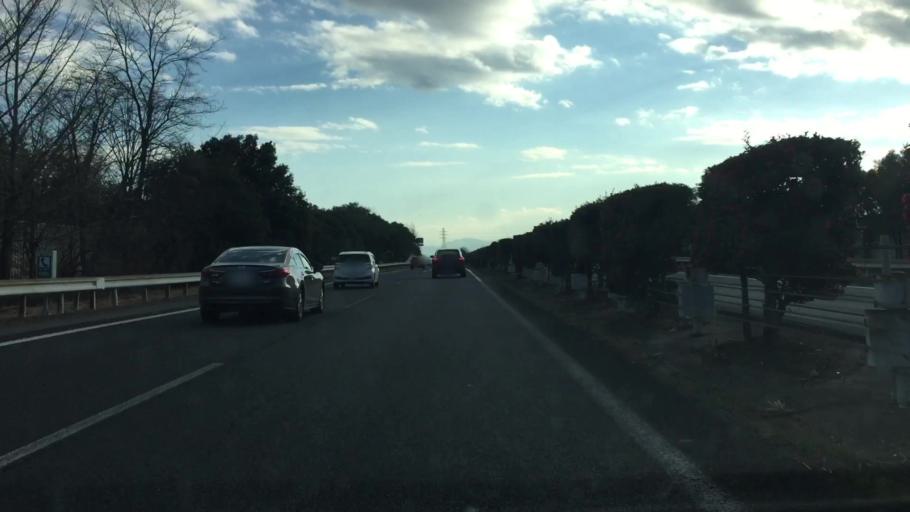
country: JP
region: Gunma
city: Kanekomachi
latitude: 36.4428
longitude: 139.0147
